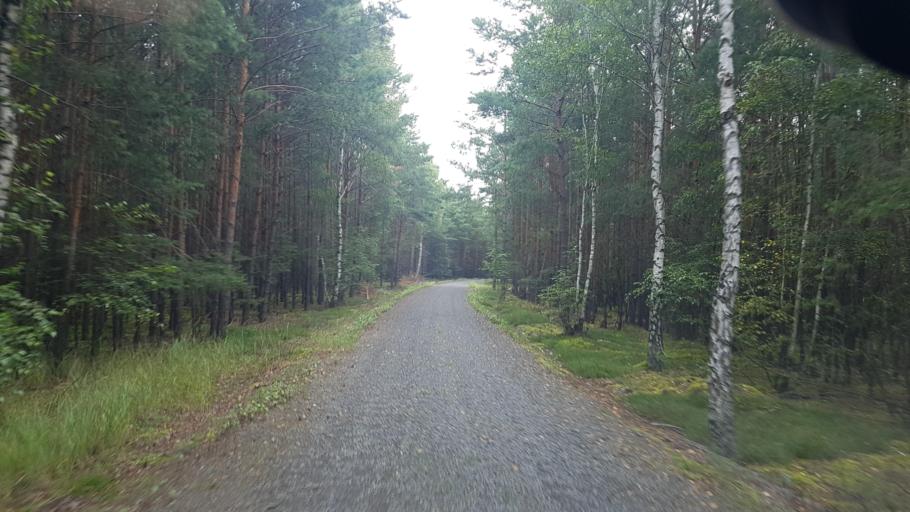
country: DE
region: Brandenburg
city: Grossraschen
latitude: 51.6286
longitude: 13.9907
